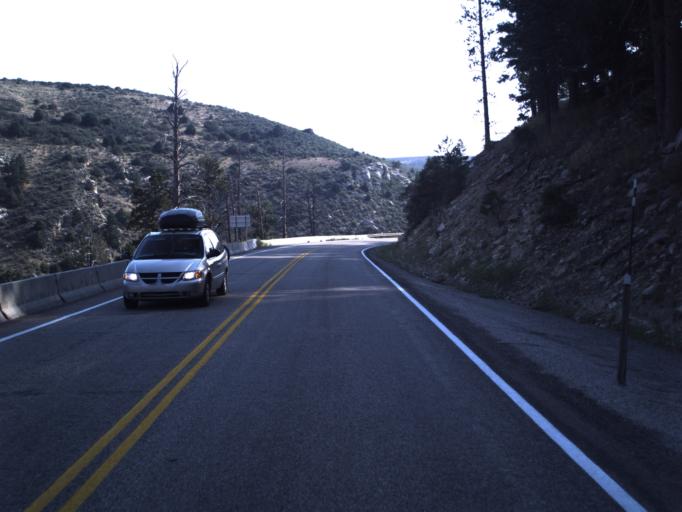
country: US
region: Utah
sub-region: Uintah County
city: Maeser
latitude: 40.6587
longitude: -109.4885
